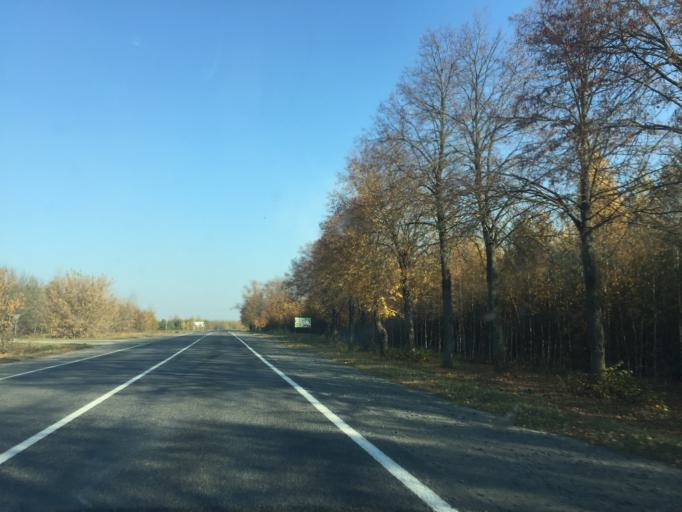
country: BY
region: Gomel
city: Dobrush
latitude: 52.3882
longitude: 31.4520
